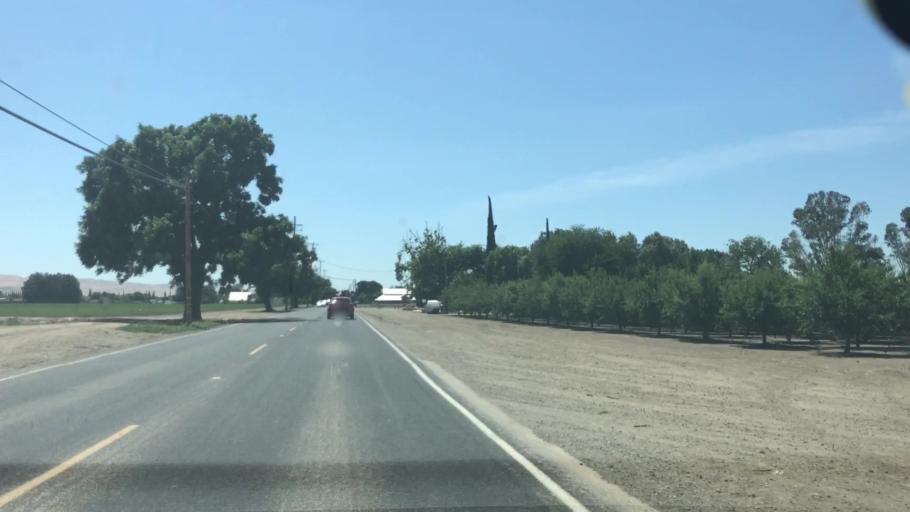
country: US
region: California
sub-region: San Joaquin County
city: Tracy
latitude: 37.7252
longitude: -121.4053
